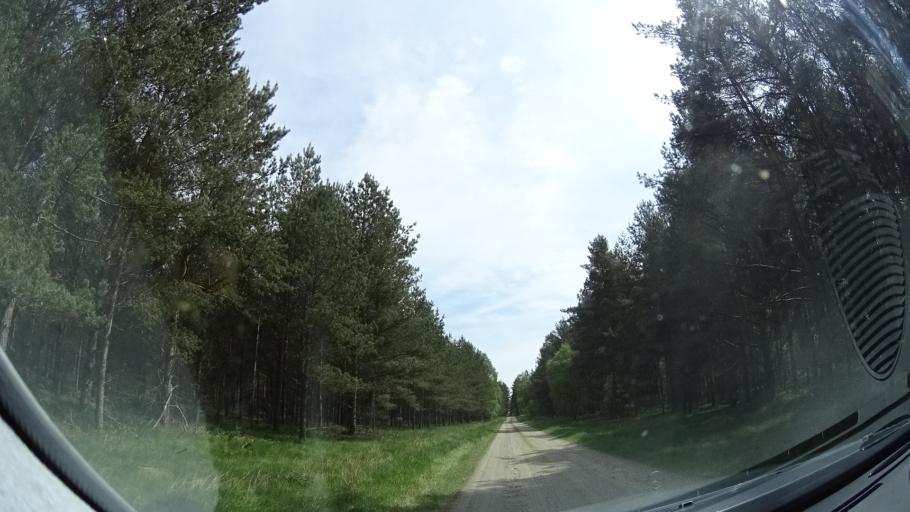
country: SE
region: Skane
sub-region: Sjobo Kommun
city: Sjoebo
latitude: 55.6703
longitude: 13.6389
